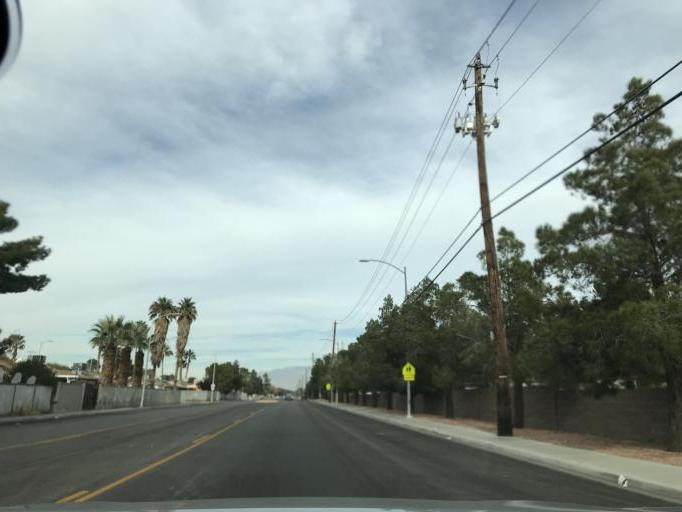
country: US
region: Nevada
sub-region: Clark County
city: Las Vegas
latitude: 36.2037
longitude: -115.2148
